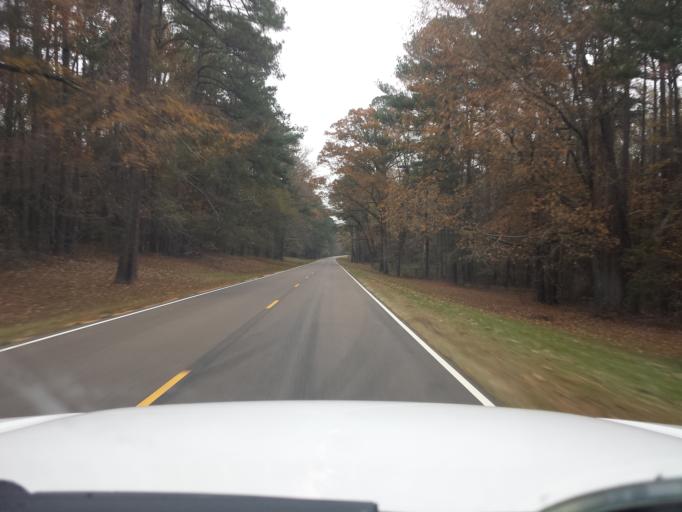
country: US
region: Mississippi
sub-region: Madison County
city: Canton
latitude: 32.5337
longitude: -89.9621
